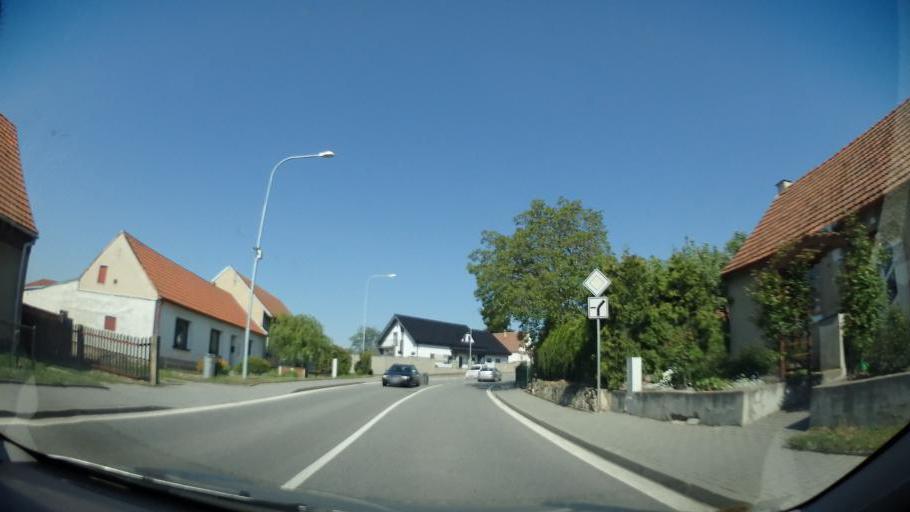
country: CZ
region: South Moravian
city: Zbraslav
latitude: 49.1810
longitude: 16.2913
